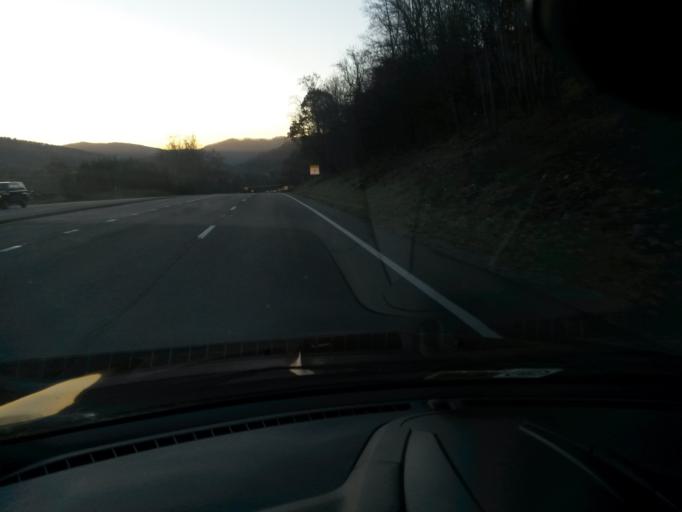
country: US
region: Virginia
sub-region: Roanoke County
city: Narrows
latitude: 37.2142
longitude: -79.9592
